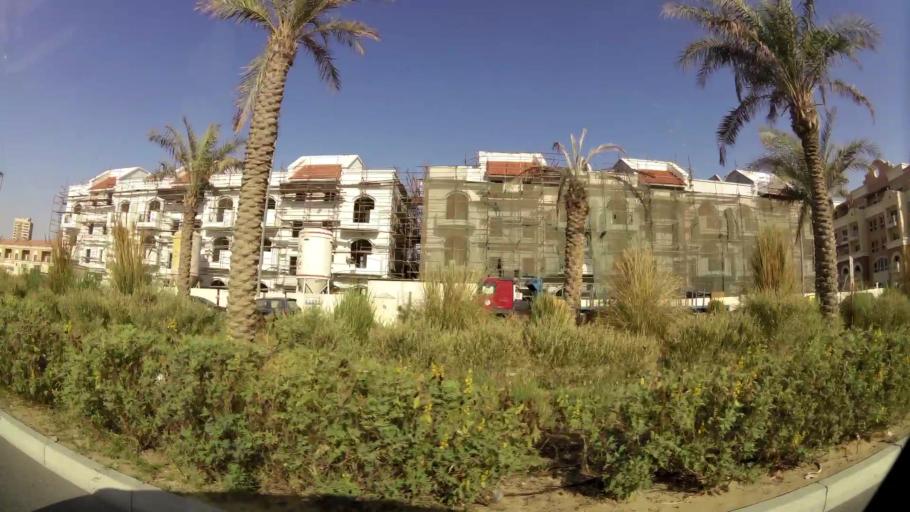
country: AE
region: Dubai
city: Dubai
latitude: 25.0531
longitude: 55.2147
